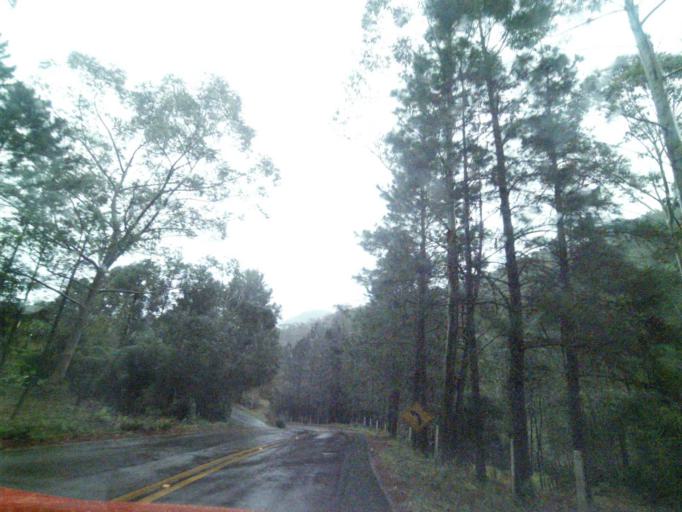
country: BR
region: Santa Catarina
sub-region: Anitapolis
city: Anitapolis
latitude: -27.7974
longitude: -49.0450
